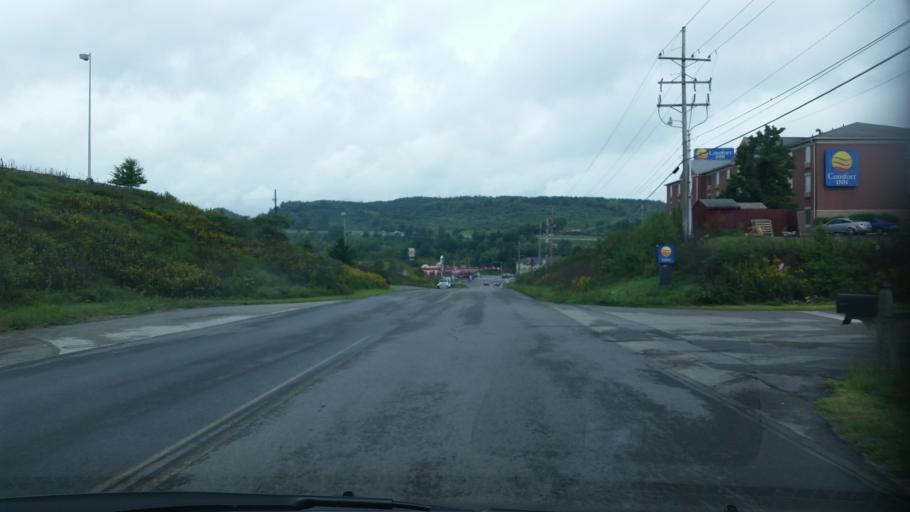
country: US
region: Pennsylvania
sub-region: Clearfield County
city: Clearfield
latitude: 41.0344
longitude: -78.3964
